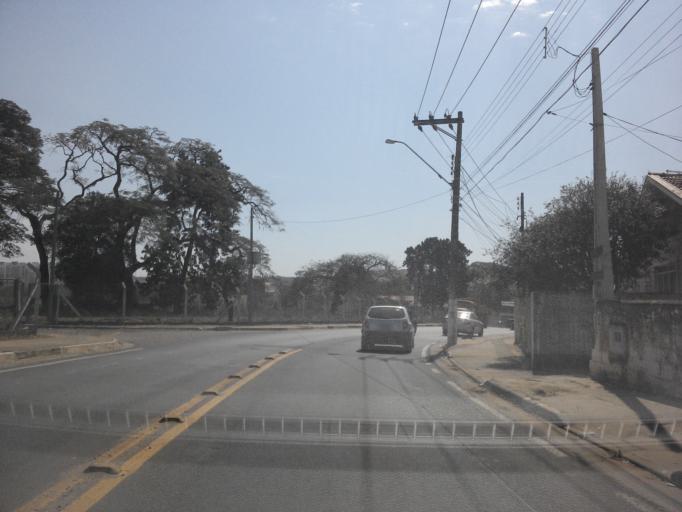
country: BR
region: Sao Paulo
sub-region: Hortolandia
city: Hortolandia
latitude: -22.8654
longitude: -47.2247
